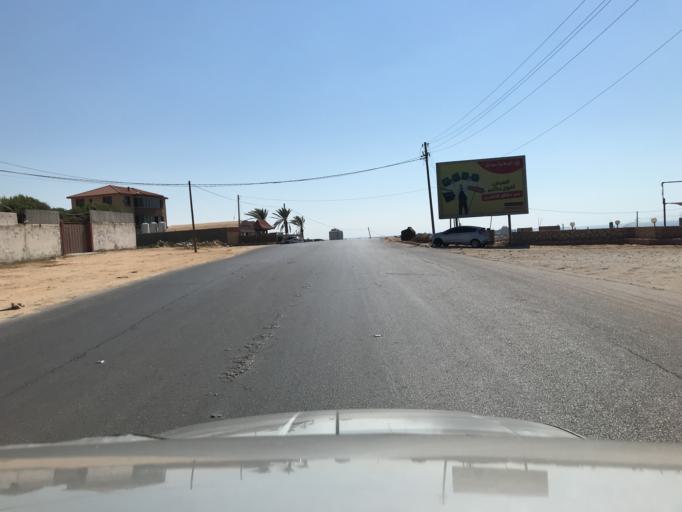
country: PS
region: Gaza Strip
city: Az Zuwaydah
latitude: 31.4569
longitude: 34.3700
